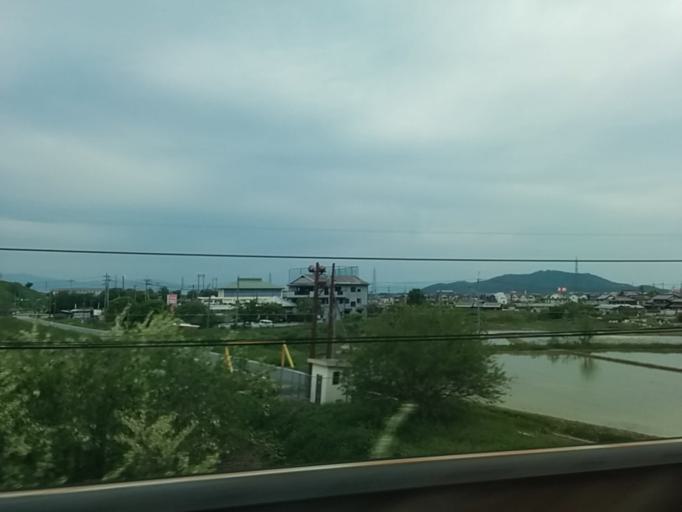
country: JP
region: Shiga Prefecture
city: Hikone
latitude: 35.1881
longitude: 136.2227
